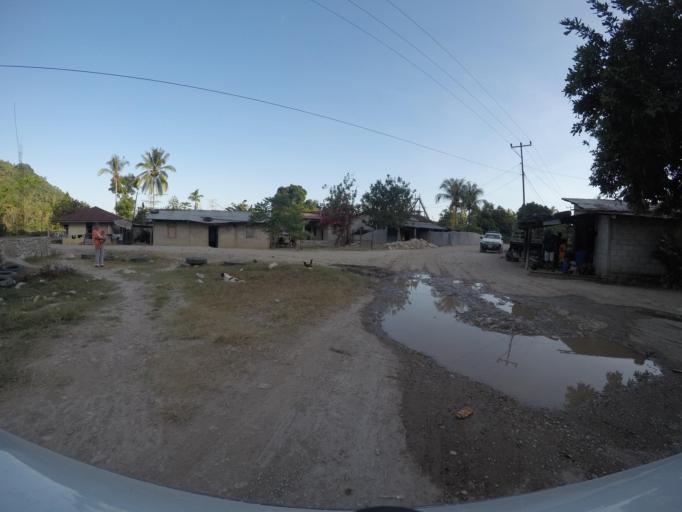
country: TL
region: Viqueque
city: Viqueque
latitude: -8.7952
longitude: 126.5574
